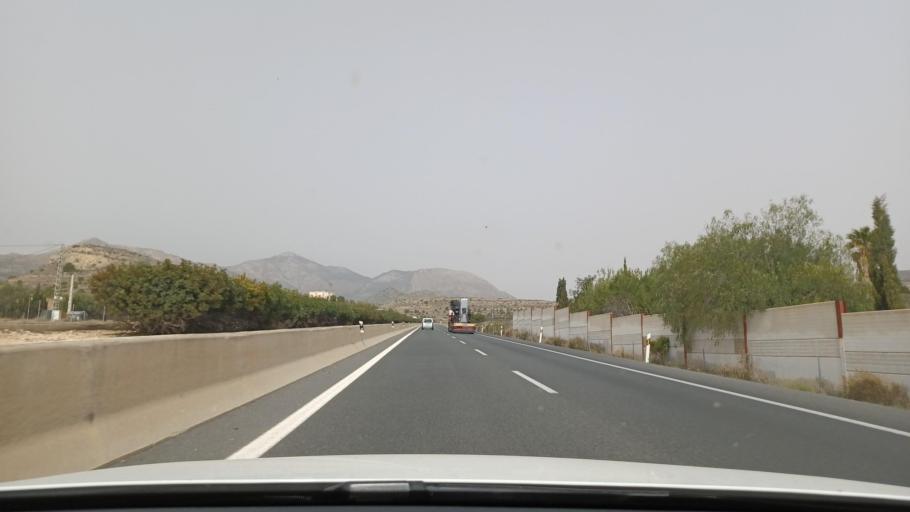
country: ES
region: Valencia
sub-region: Provincia de Alicante
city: Agost
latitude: 38.4579
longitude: -0.5739
